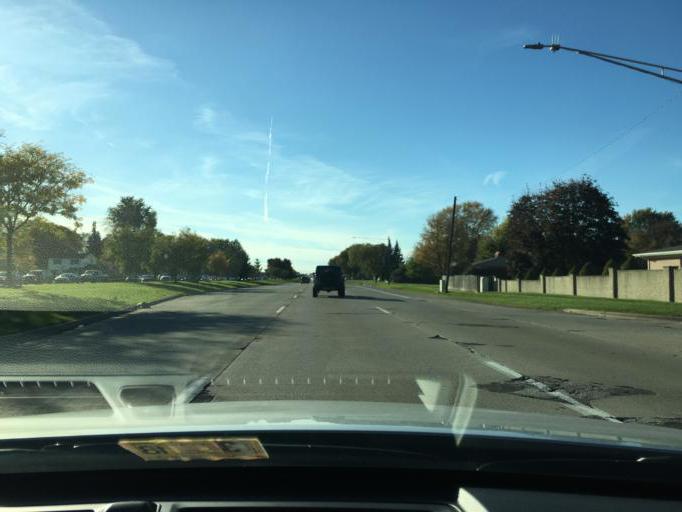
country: US
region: Michigan
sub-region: Macomb County
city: Sterling Heights
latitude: 42.5663
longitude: -83.0186
